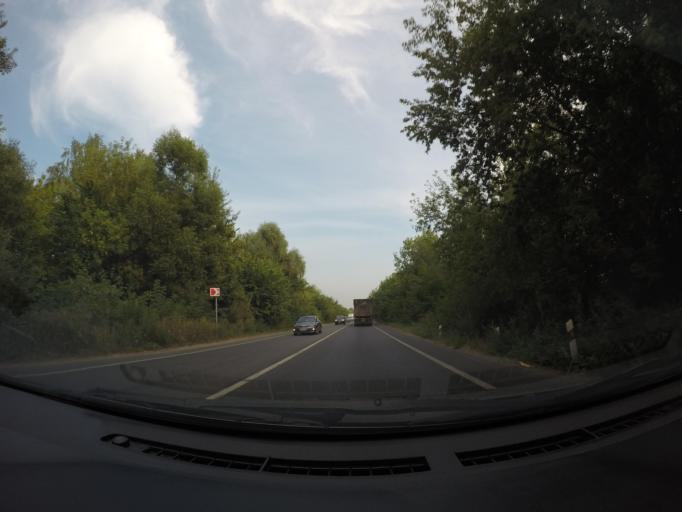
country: RU
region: Moskovskaya
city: Rechitsy
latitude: 55.5876
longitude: 38.5373
